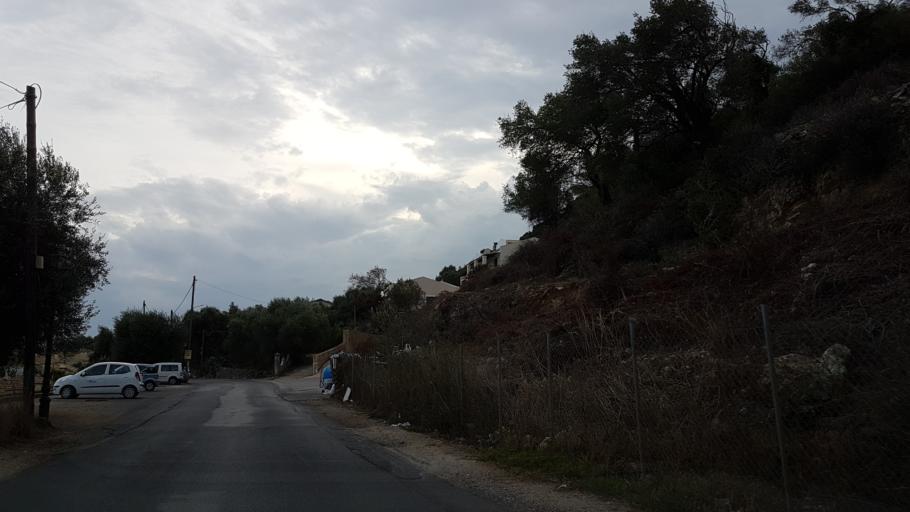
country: GR
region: Ionian Islands
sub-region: Nomos Kerkyras
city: Kontokali
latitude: 39.7184
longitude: 19.8669
